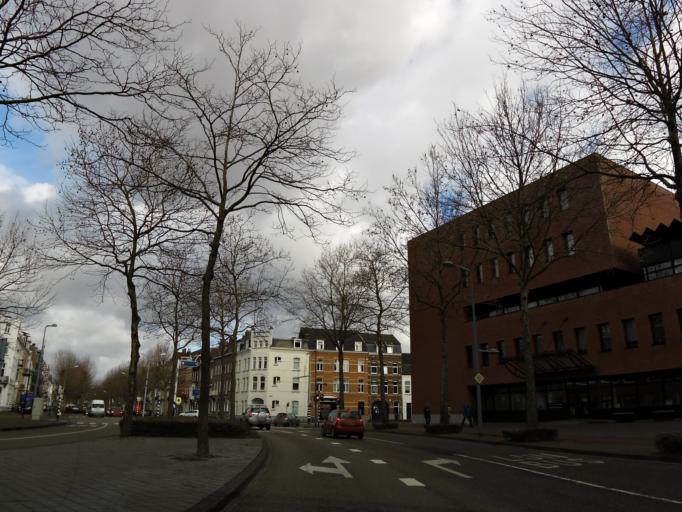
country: NL
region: Limburg
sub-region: Gemeente Maastricht
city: Maastricht
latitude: 50.8467
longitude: 5.7032
